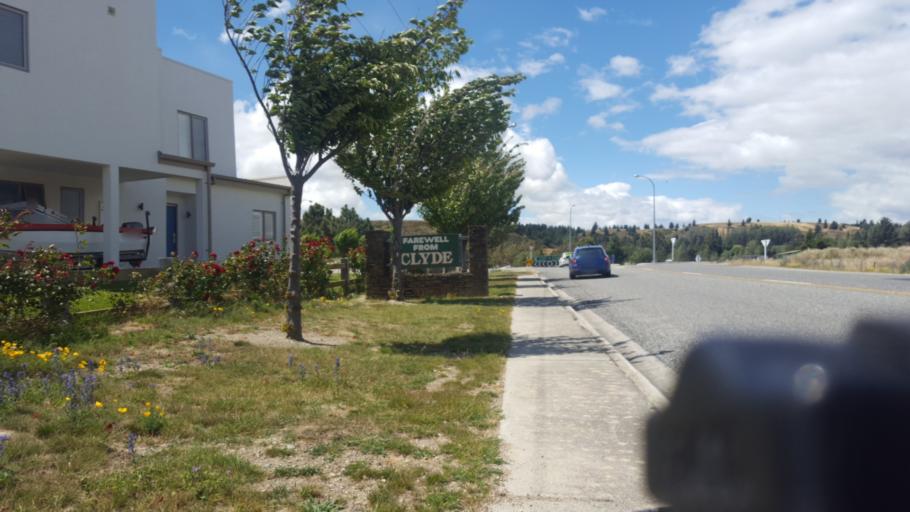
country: NZ
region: Otago
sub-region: Queenstown-Lakes District
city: Wanaka
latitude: -45.1977
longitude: 169.3353
